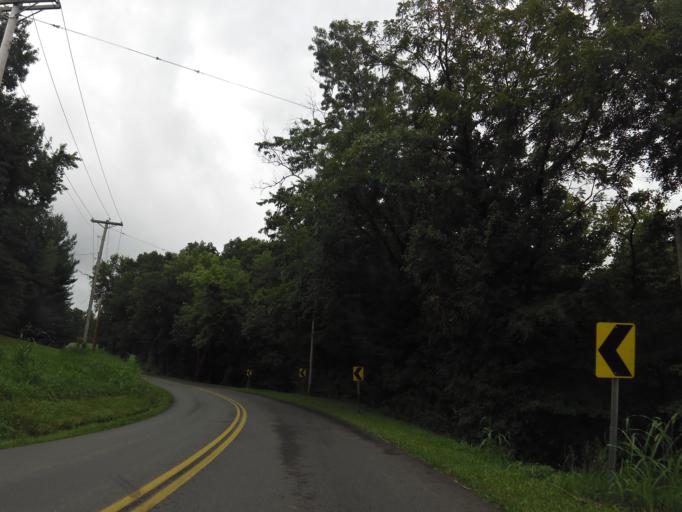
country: US
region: Missouri
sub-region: Cape Girardeau County
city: Cape Girardeau
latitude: 37.3553
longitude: -89.5628
